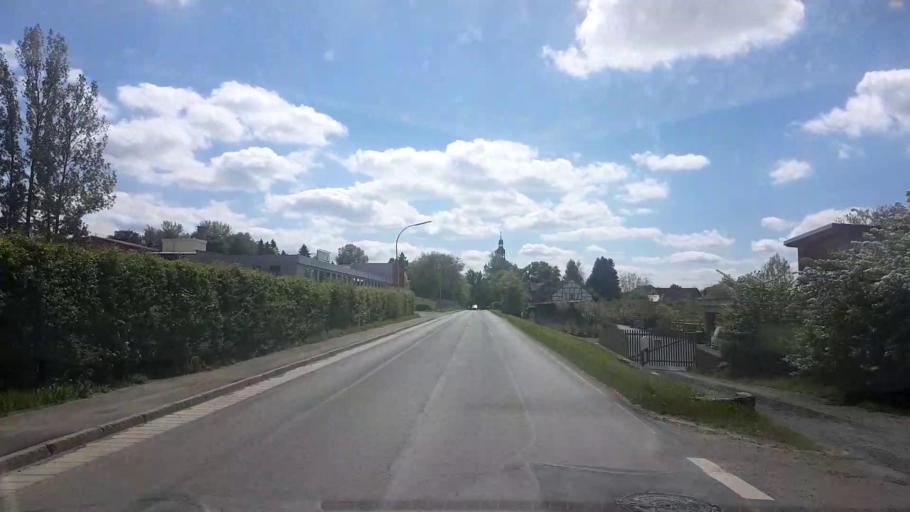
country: DE
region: Bavaria
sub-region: Upper Franconia
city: Grossheirath
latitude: 50.1803
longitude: 10.9514
